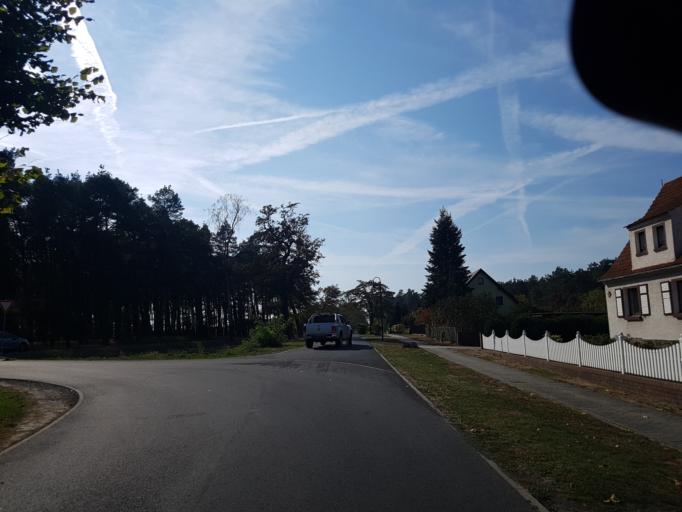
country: DE
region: Brandenburg
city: Hohenbucko
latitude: 51.7607
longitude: 13.4649
